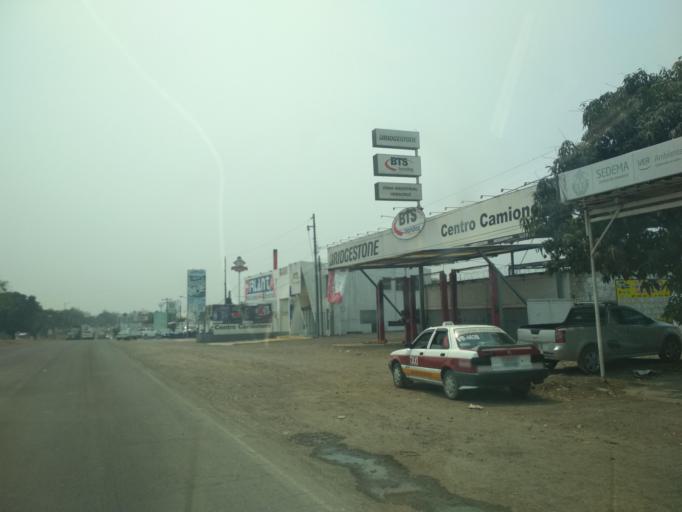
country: MX
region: Veracruz
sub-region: Veracruz
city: Lomas de Rio Medio Cuatro
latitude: 19.1690
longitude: -96.2245
